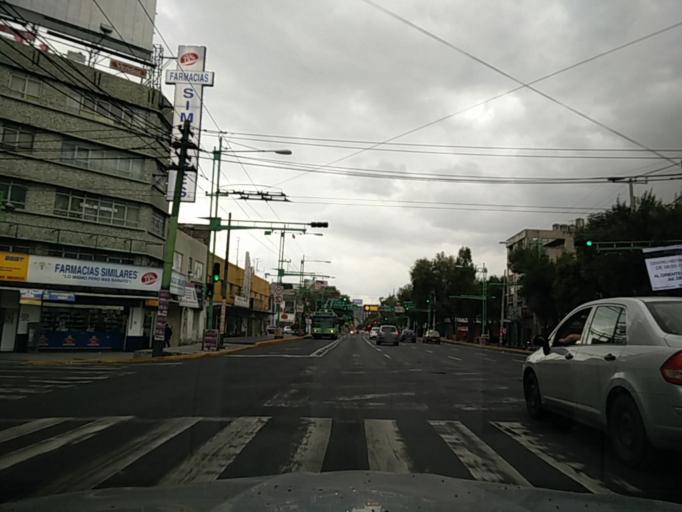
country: MX
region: Mexico City
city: Mexico City
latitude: 19.4151
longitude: -99.1439
